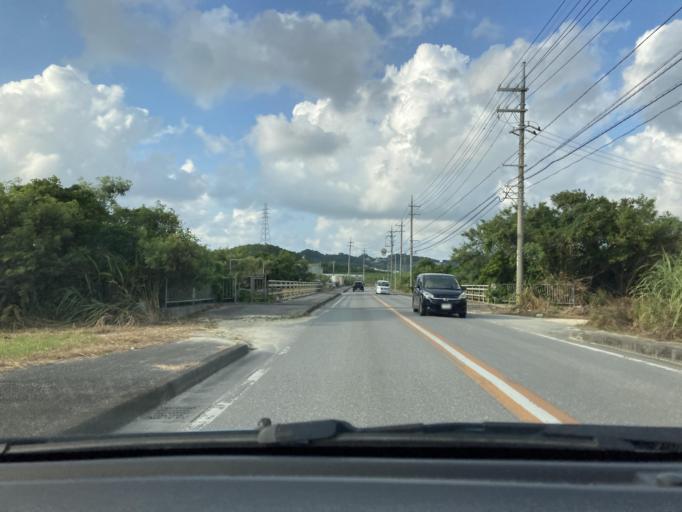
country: JP
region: Okinawa
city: Itoman
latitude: 26.1392
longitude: 127.7005
